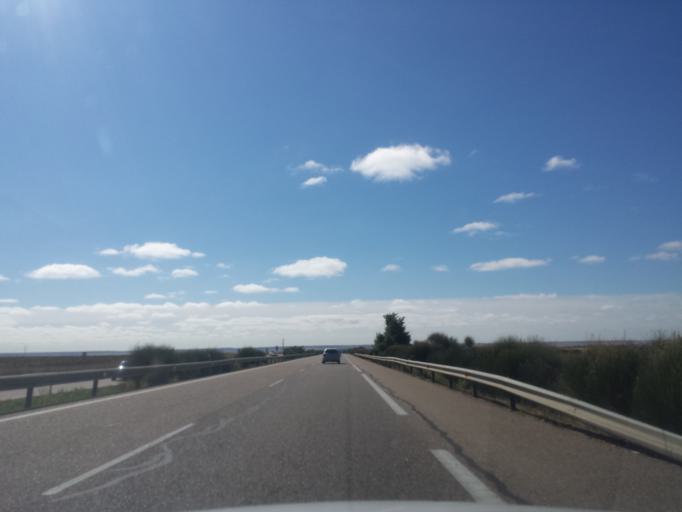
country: ES
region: Castille and Leon
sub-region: Provincia de Zamora
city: Quintanilla del Monte
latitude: 41.8146
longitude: -5.3625
